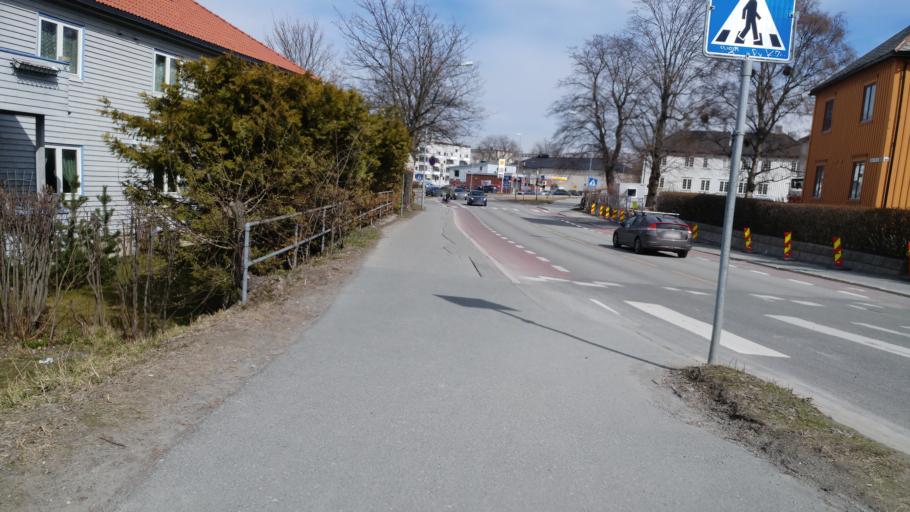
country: NO
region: Sor-Trondelag
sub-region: Trondheim
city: Trondheim
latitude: 63.4355
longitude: 10.4291
